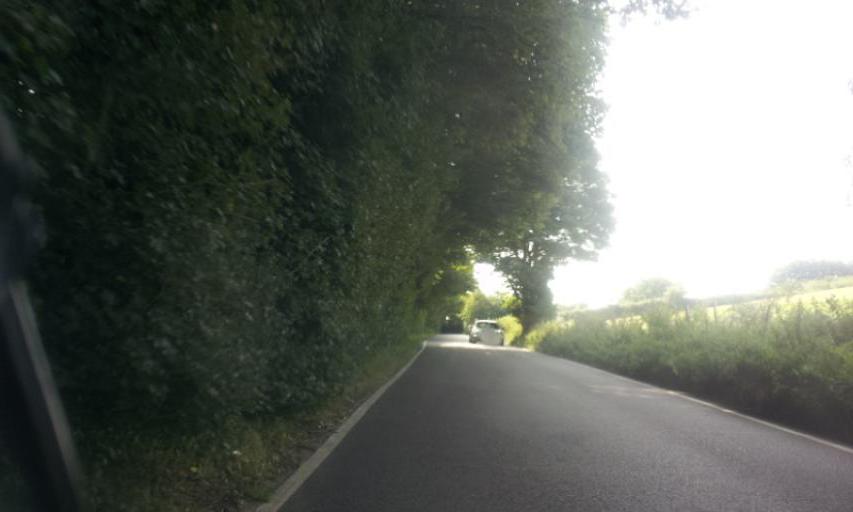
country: GB
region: England
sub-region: Kent
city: Boxley
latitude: 51.3430
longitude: 0.5640
